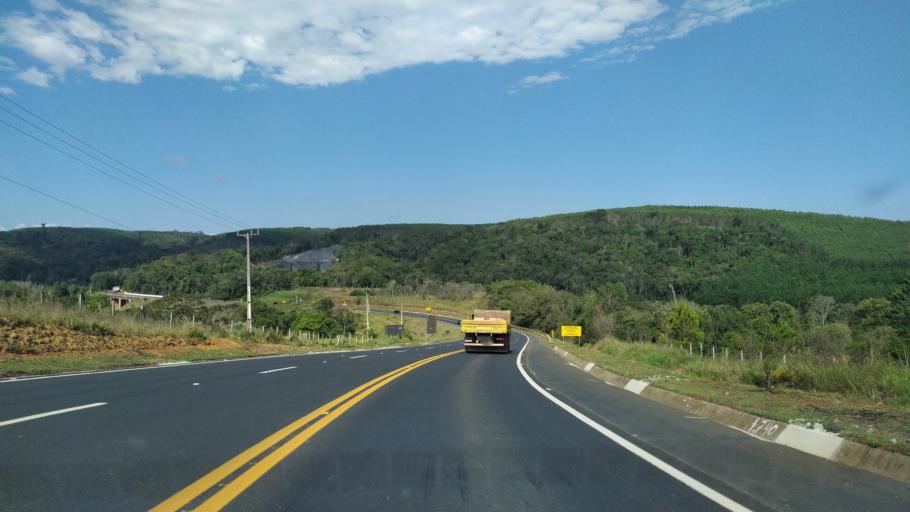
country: BR
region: Parana
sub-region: Telemaco Borba
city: Telemaco Borba
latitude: -24.2873
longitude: -50.7050
